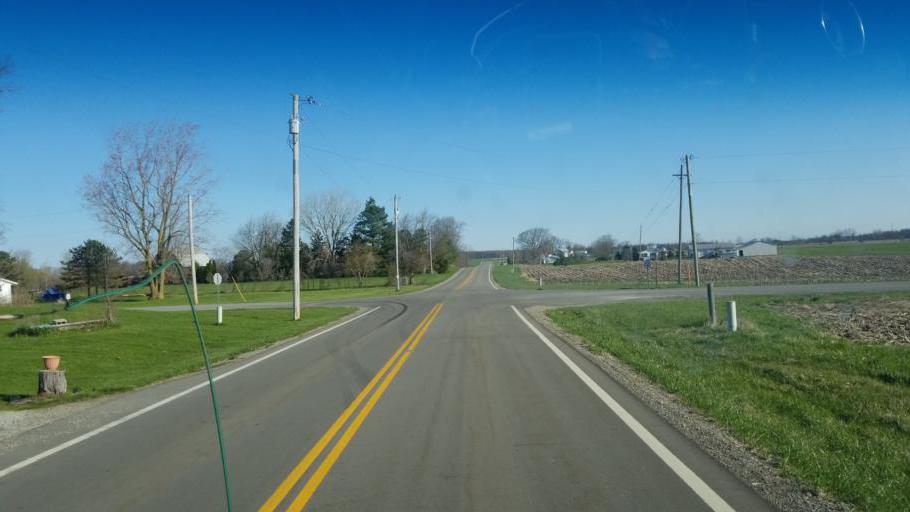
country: US
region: Ohio
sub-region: Logan County
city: Northwood
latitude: 40.5001
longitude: -83.6362
